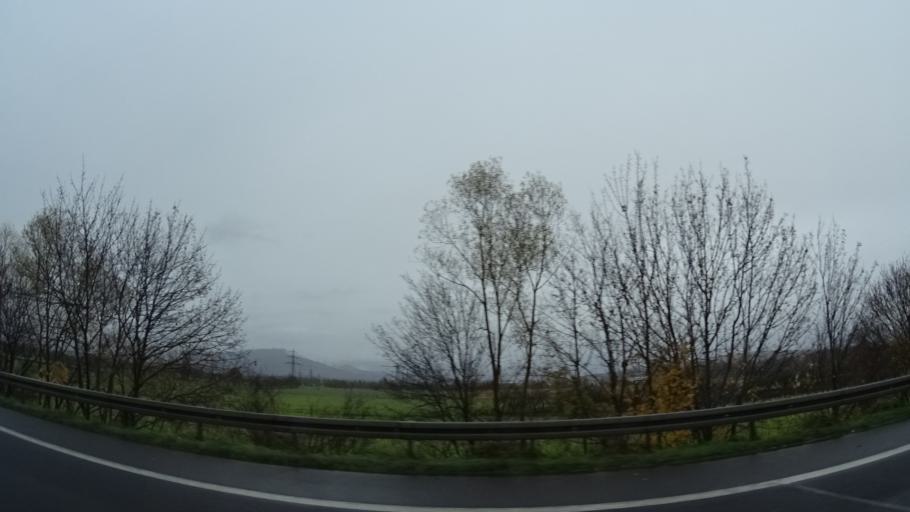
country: DE
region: Baden-Wuerttemberg
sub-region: Karlsruhe Region
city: Rastatt
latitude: 48.8466
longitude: 8.2327
